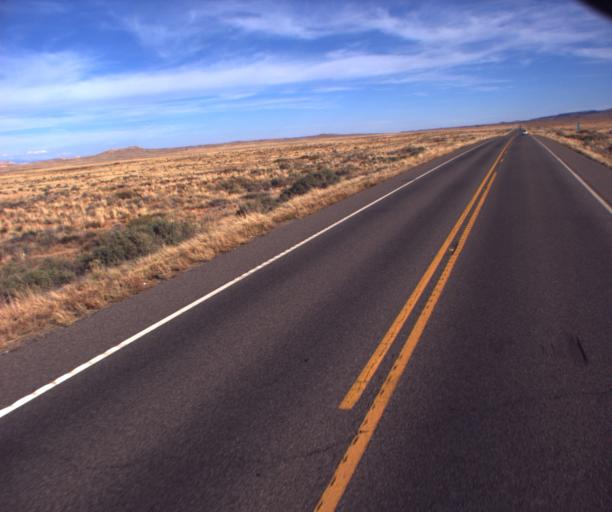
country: US
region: Arizona
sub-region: Apache County
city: Lukachukai
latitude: 36.9502
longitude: -109.2820
